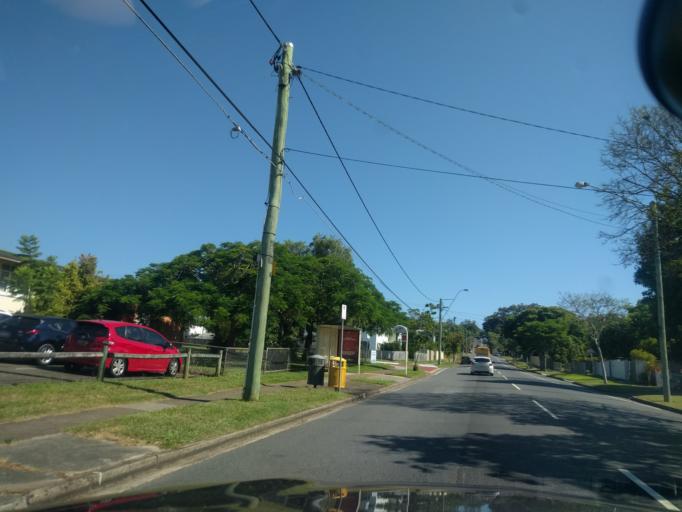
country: AU
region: Queensland
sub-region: Brisbane
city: Stafford
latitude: -27.4049
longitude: 153.0088
